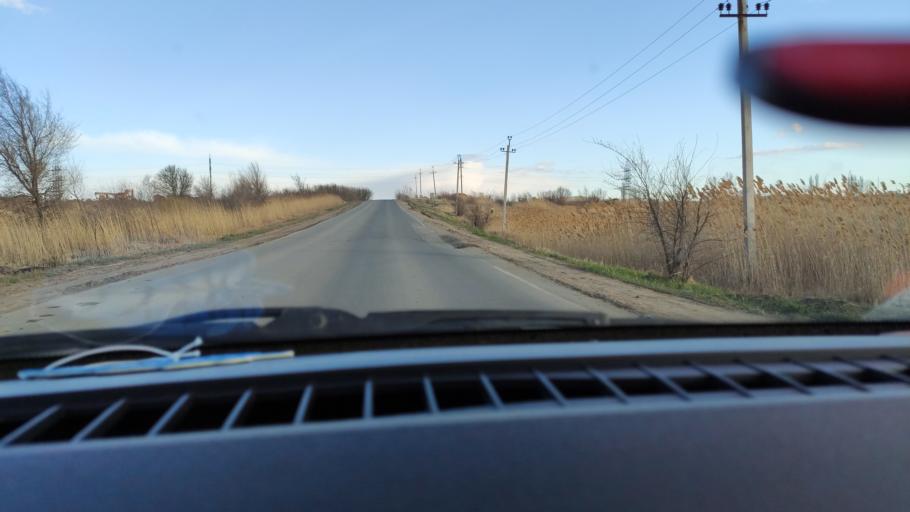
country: RU
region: Saratov
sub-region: Saratovskiy Rayon
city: Saratov
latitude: 51.6160
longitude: 45.9495
